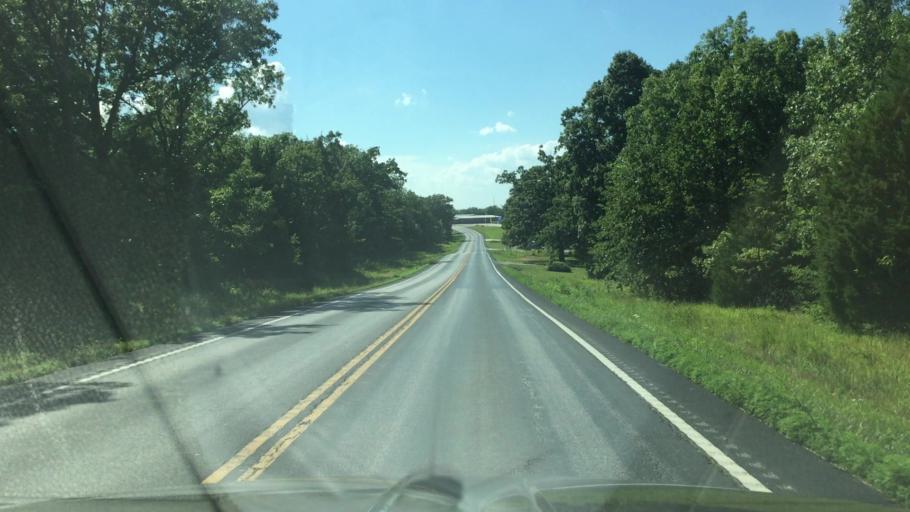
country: US
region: Missouri
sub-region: Camden County
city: Osage Beach
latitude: 38.1377
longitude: -92.5766
